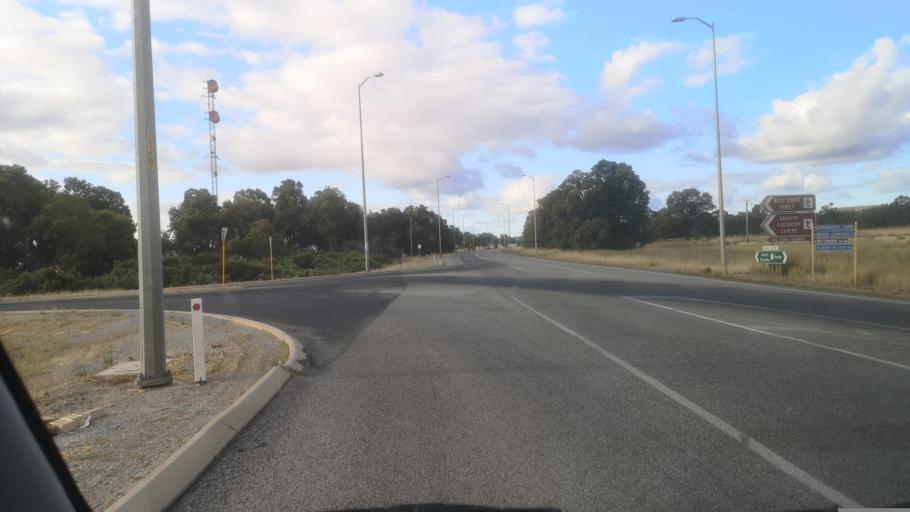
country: AU
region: Western Australia
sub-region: Wanneroo
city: Yanchep
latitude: -31.3329
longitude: 115.8682
